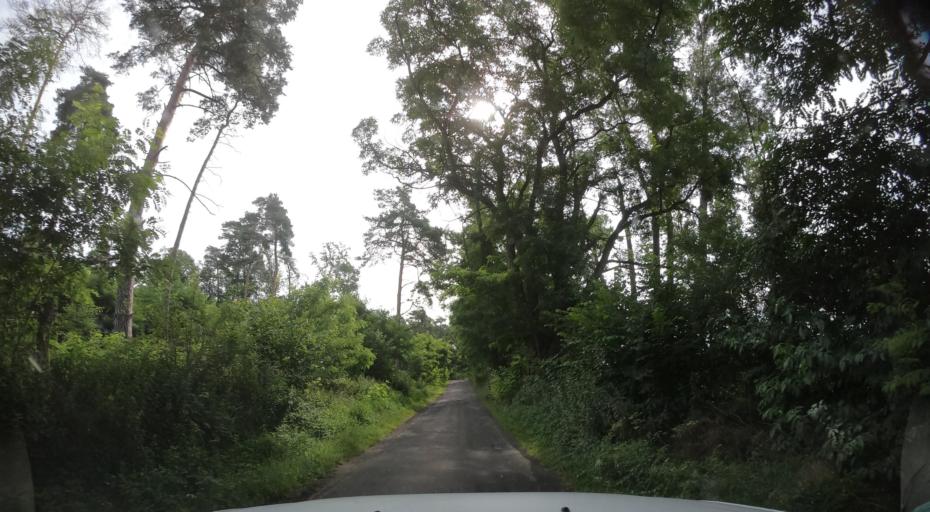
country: PL
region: West Pomeranian Voivodeship
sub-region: Powiat gryfinski
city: Mieszkowice
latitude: 52.8705
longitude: 14.5226
